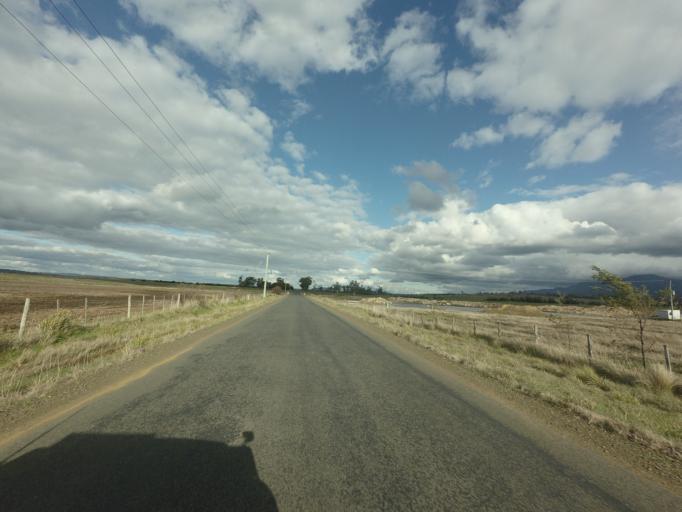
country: AU
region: Tasmania
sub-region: Northern Midlands
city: Longford
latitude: -41.8124
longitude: 147.1897
